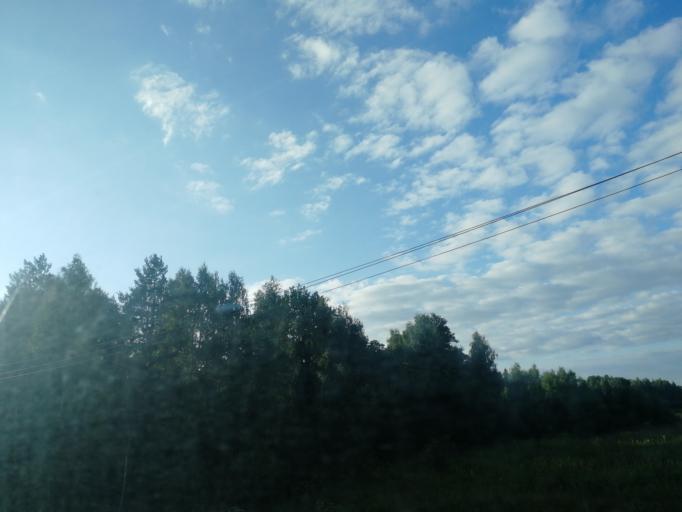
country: RU
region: Kaluga
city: Kaluga
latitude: 54.4350
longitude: 36.3544
